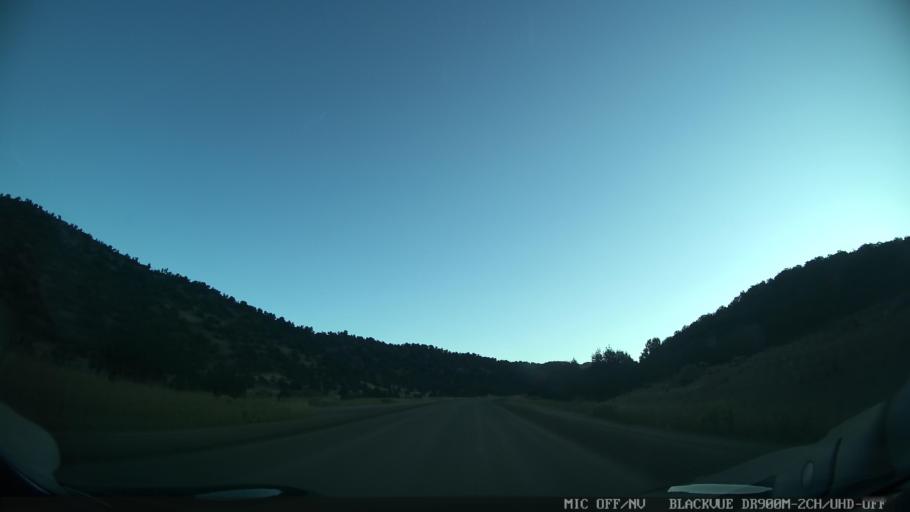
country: US
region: Colorado
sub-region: Grand County
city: Kremmling
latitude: 39.9057
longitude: -106.5856
